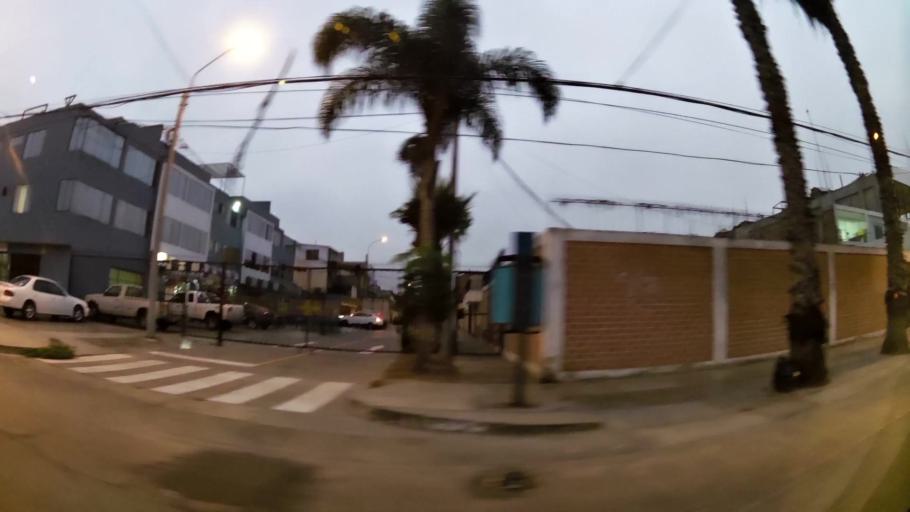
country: PE
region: Callao
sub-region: Callao
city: Callao
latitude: -12.0819
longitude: -77.0983
